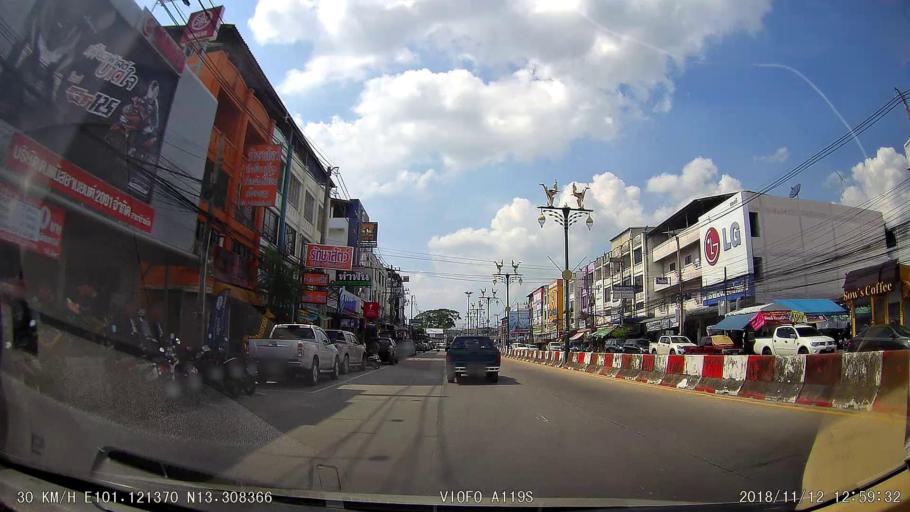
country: TH
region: Chon Buri
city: Ban Bueng
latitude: 13.3082
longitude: 101.1216
